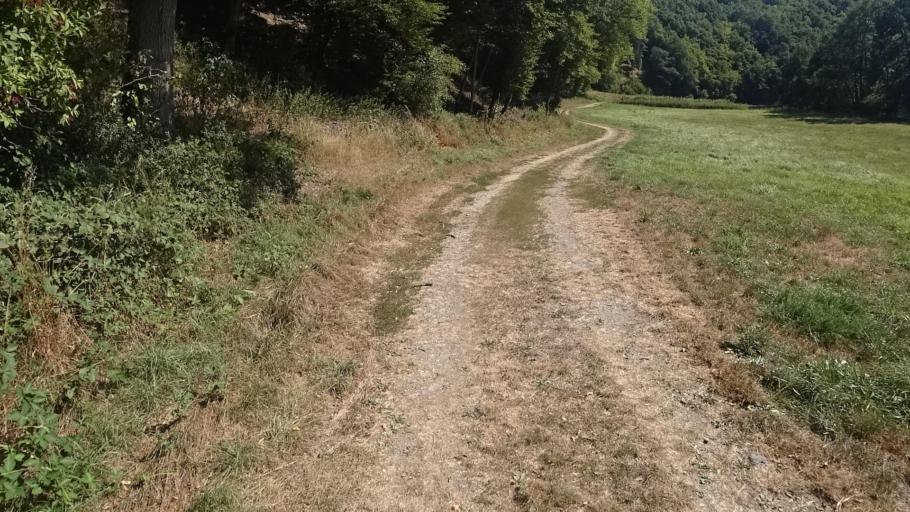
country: DE
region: Rheinland-Pfalz
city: Ravengiersburg
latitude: 49.9187
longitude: 7.4824
